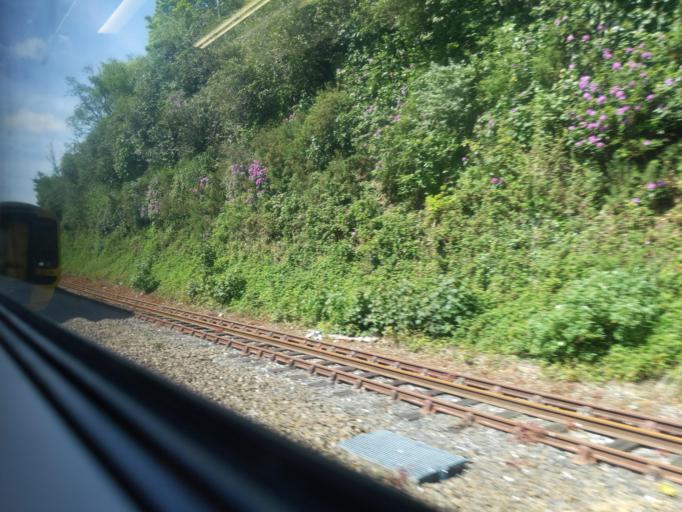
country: GB
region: England
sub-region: Cornwall
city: St Austell
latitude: 50.3386
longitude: -4.7852
